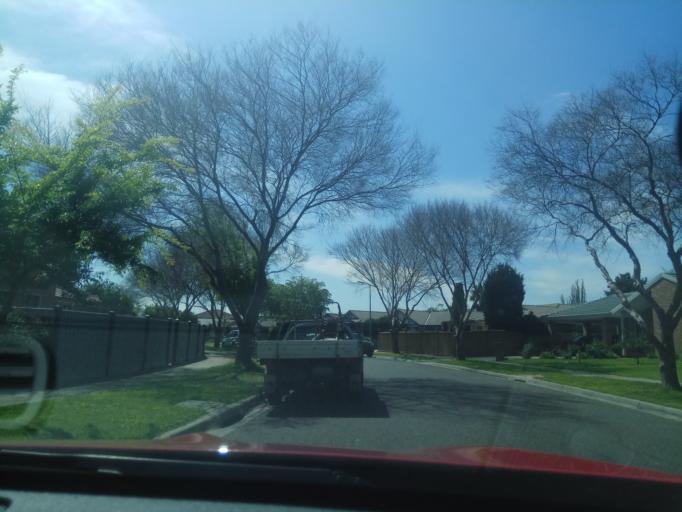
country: AU
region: Victoria
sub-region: Kingston
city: Aspendale Gardens
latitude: -38.0214
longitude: 145.1140
